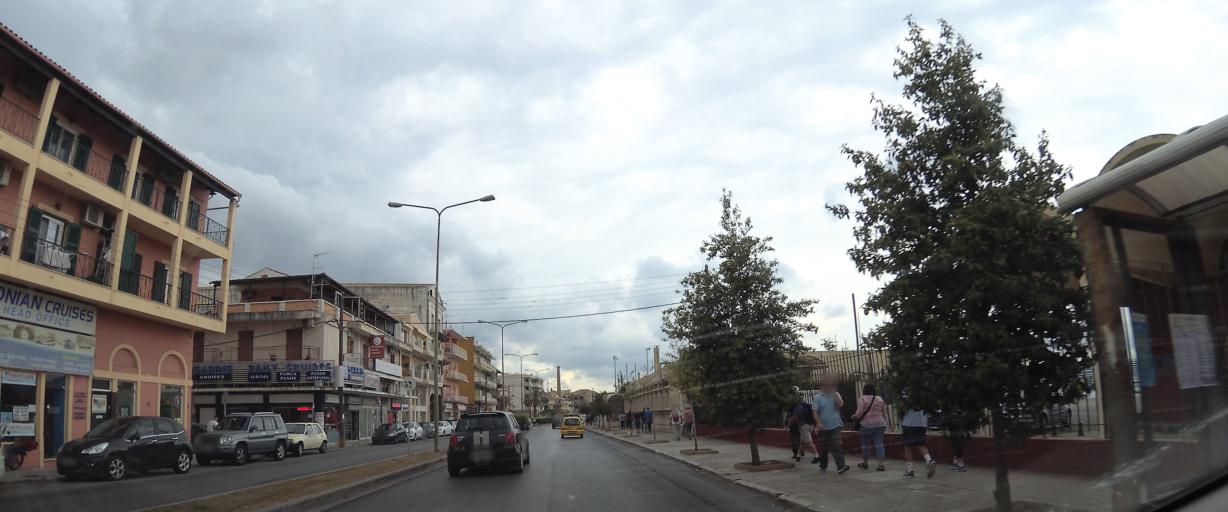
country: GR
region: Ionian Islands
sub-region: Nomos Kerkyras
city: Kerkyra
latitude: 39.6258
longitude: 19.9100
